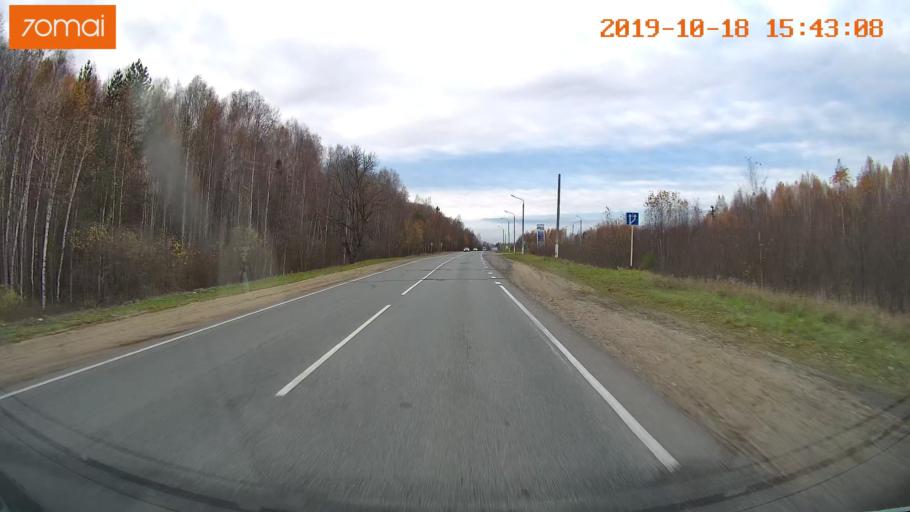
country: RU
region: Vladimir
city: Golovino
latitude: 55.9636
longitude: 40.5555
